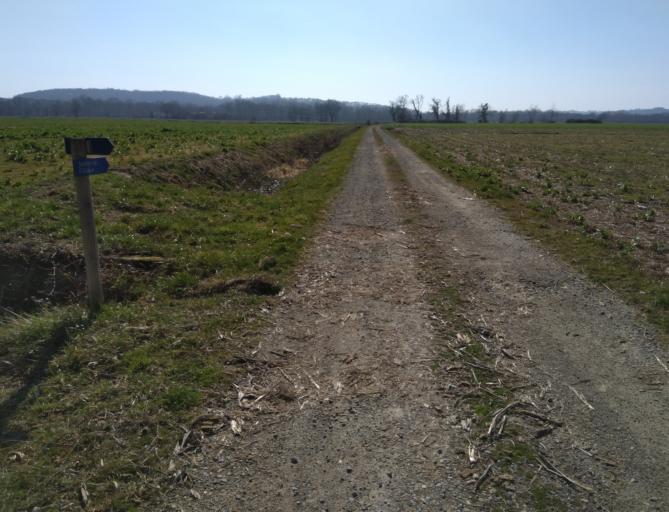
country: FR
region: Midi-Pyrenees
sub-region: Departement du Gers
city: Barcelonne-du-Gers
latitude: 43.6934
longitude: -0.2073
